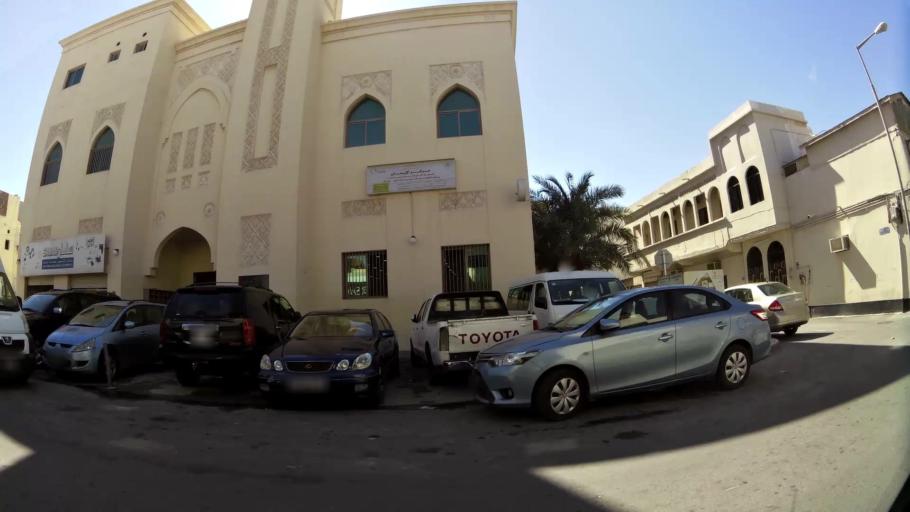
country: BH
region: Muharraq
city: Al Muharraq
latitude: 26.2474
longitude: 50.6141
